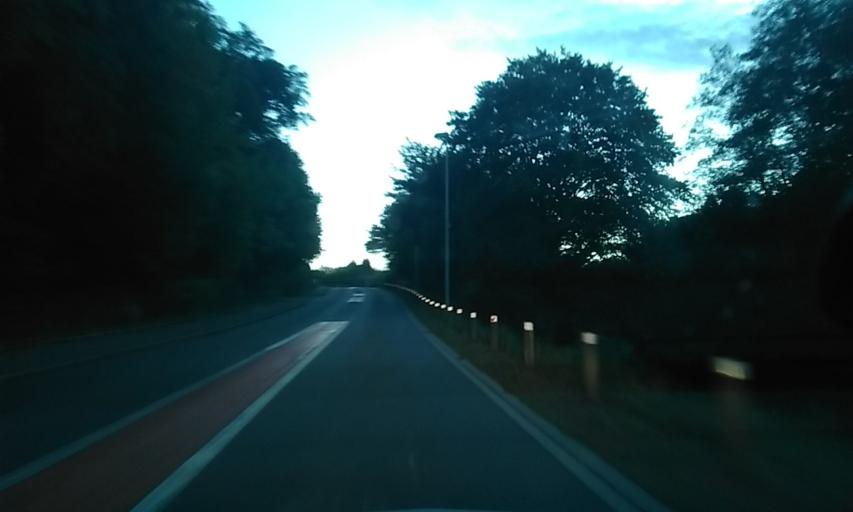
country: FR
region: Brittany
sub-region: Departement d'Ille-et-Vilaine
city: Saint-Thurial
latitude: 48.0321
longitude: -1.9302
